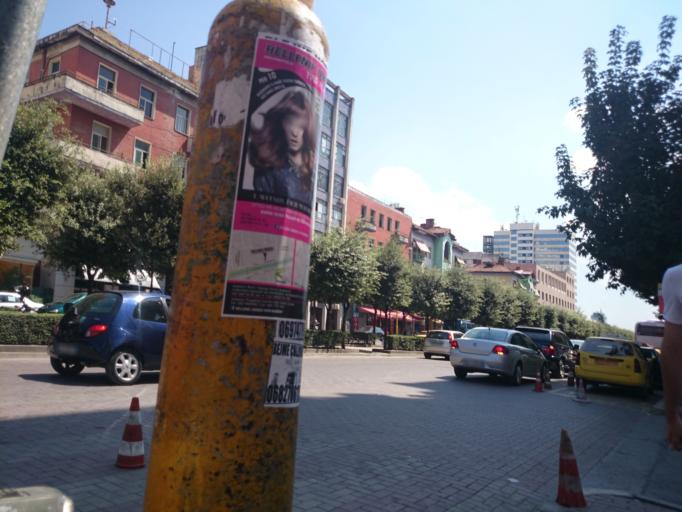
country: AL
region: Tirane
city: Tirana
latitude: 41.3320
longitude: 19.8172
